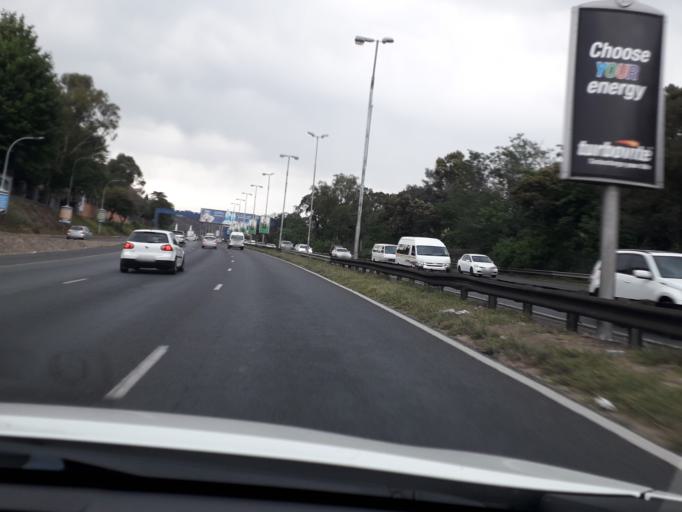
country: ZA
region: Gauteng
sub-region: City of Johannesburg Metropolitan Municipality
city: Johannesburg
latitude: -26.1489
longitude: 28.0574
